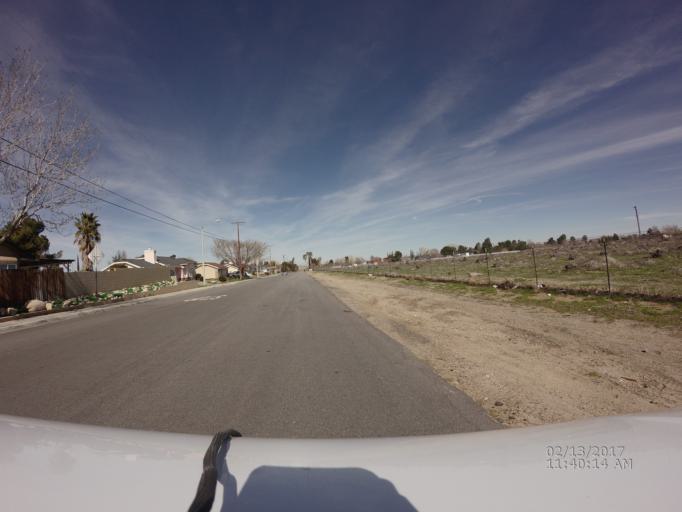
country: US
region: California
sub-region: Los Angeles County
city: Littlerock
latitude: 34.5231
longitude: -117.9969
